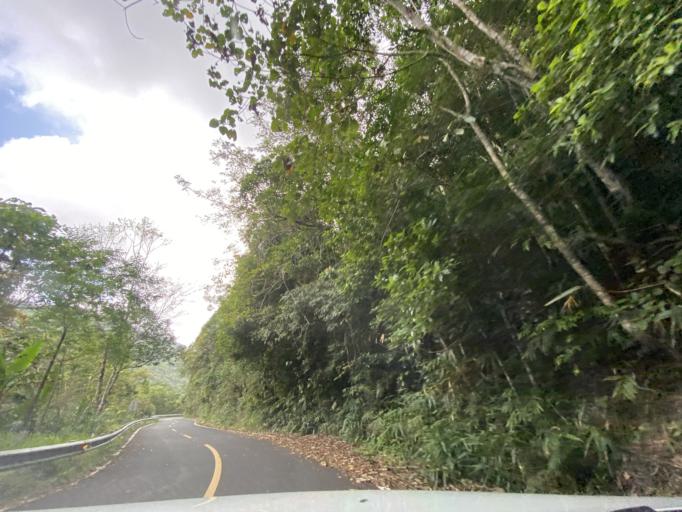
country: CN
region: Hainan
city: Diaoluoshan
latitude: 18.7046
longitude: 109.8820
